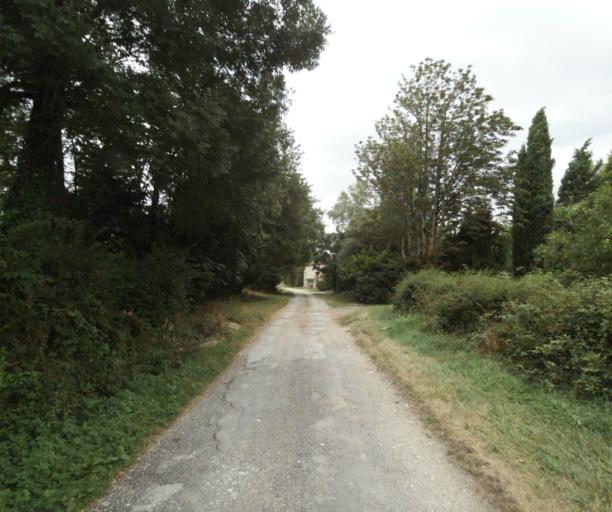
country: FR
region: Midi-Pyrenees
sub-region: Departement du Tarn
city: Soreze
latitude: 43.4609
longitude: 2.0534
